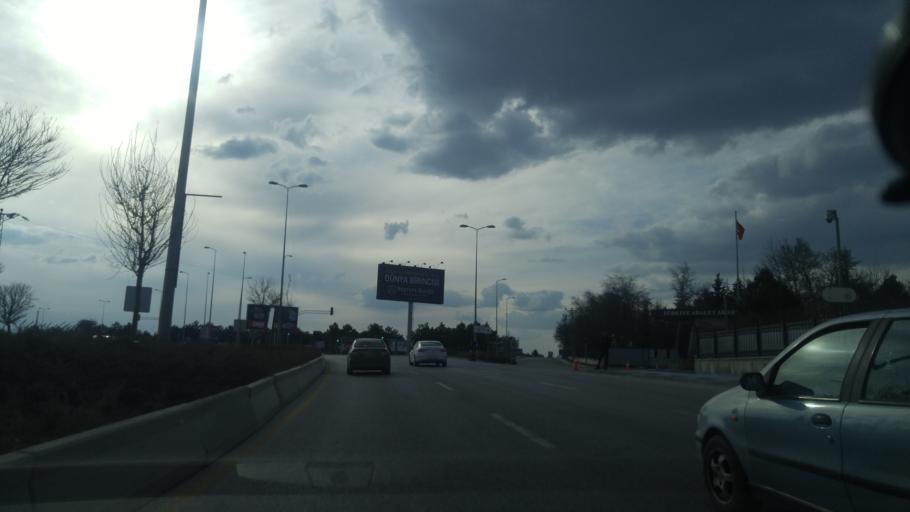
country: TR
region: Ankara
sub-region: Goelbasi
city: Golbasi
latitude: 39.8443
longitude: 32.7836
